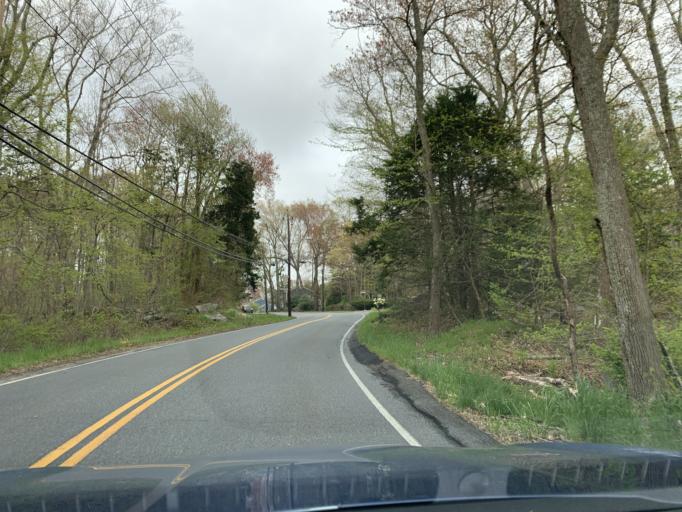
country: US
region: Rhode Island
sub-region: Washington County
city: North Kingstown
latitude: 41.5888
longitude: -71.4636
